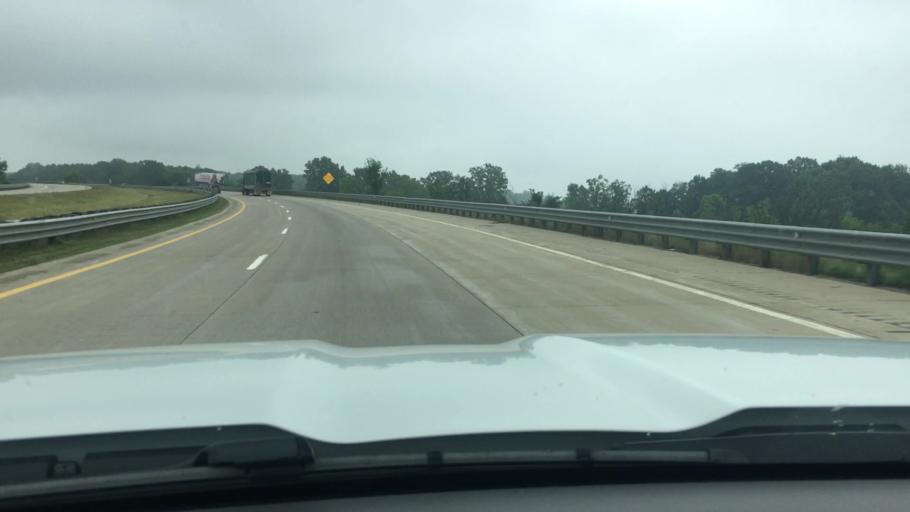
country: US
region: Michigan
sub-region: Genesee County
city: Swartz Creek
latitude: 42.9642
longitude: -83.7997
